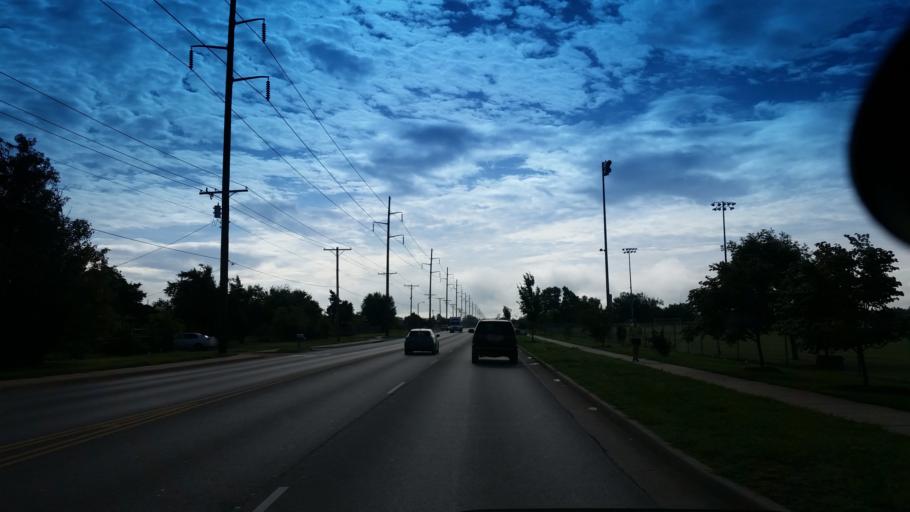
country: US
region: Oklahoma
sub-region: Oklahoma County
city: Edmond
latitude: 35.6675
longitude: -97.5030
